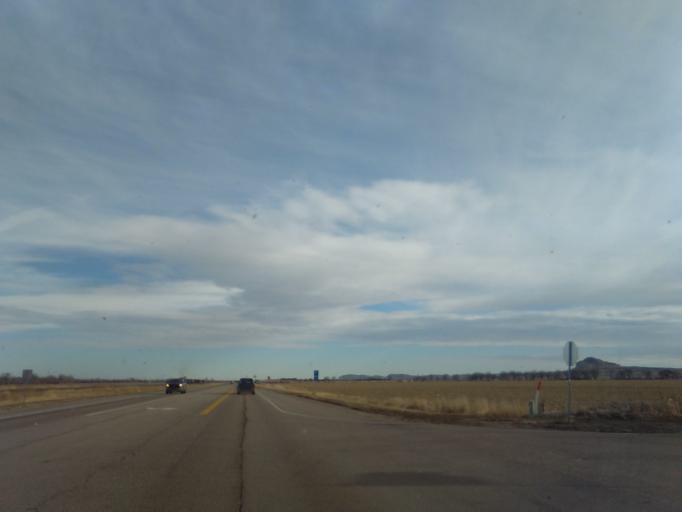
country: US
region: Nebraska
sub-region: Scotts Bluff County
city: Gering
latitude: 41.7830
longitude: -103.5155
